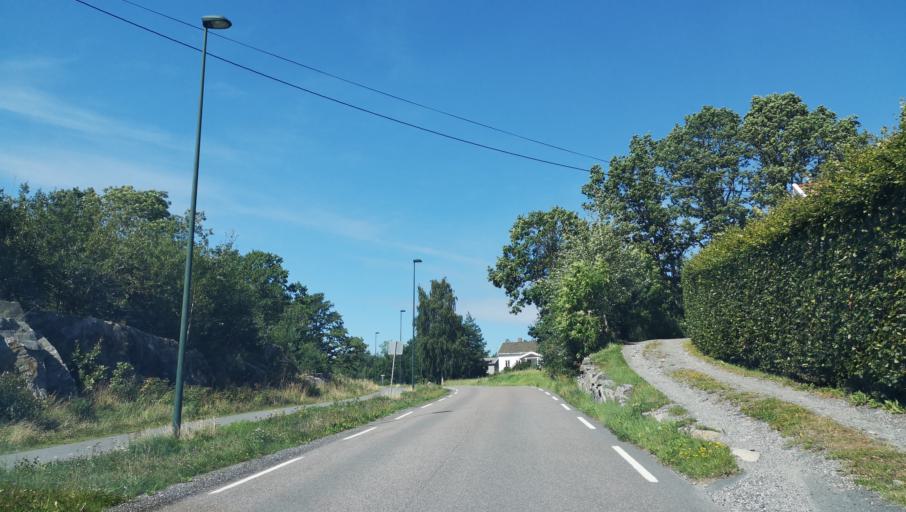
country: NO
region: Akershus
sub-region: Vestby
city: Vestby
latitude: 59.5294
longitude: 10.6883
